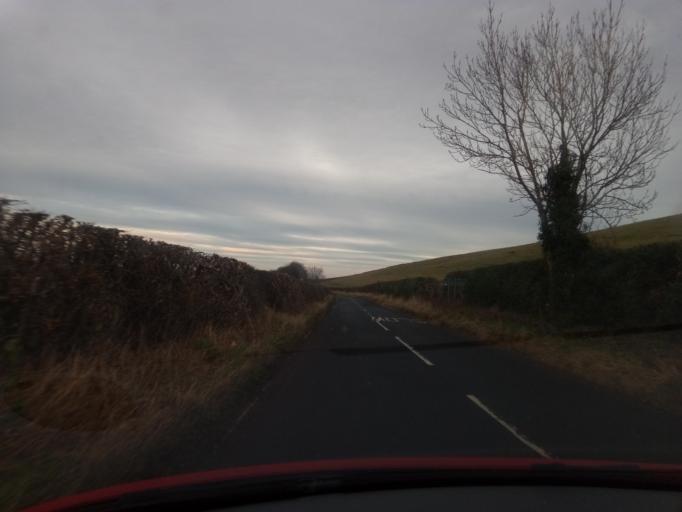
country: GB
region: England
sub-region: Northumberland
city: Kirknewton
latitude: 55.5658
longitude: -2.1349
